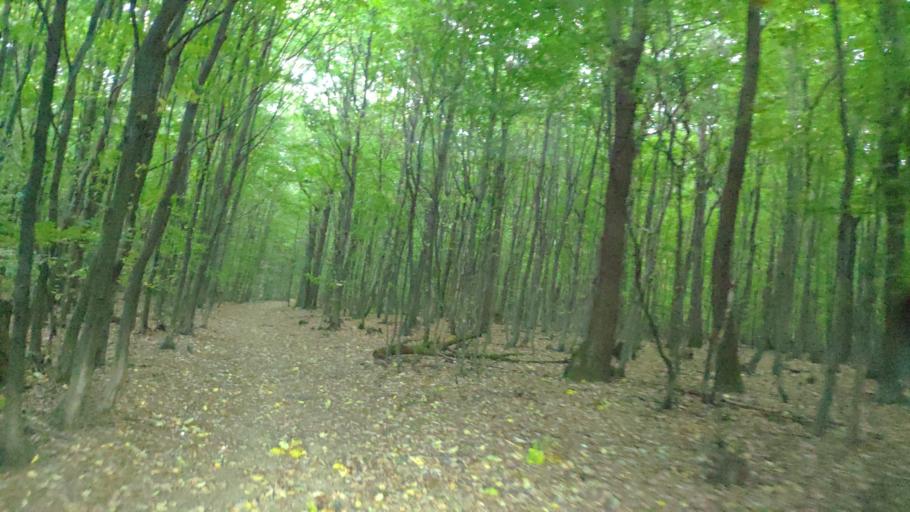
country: SK
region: Kosicky
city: Kosice
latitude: 48.7013
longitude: 21.1921
